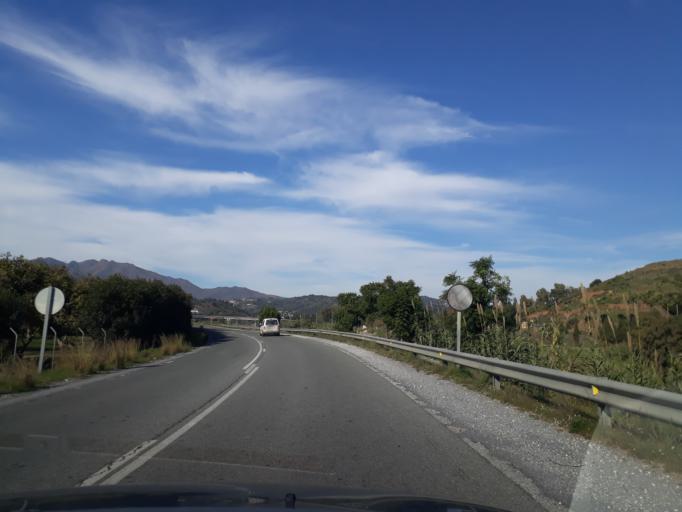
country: ES
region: Andalusia
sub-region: Provincia de Malaga
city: Fuengirola
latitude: 36.5463
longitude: -4.6891
